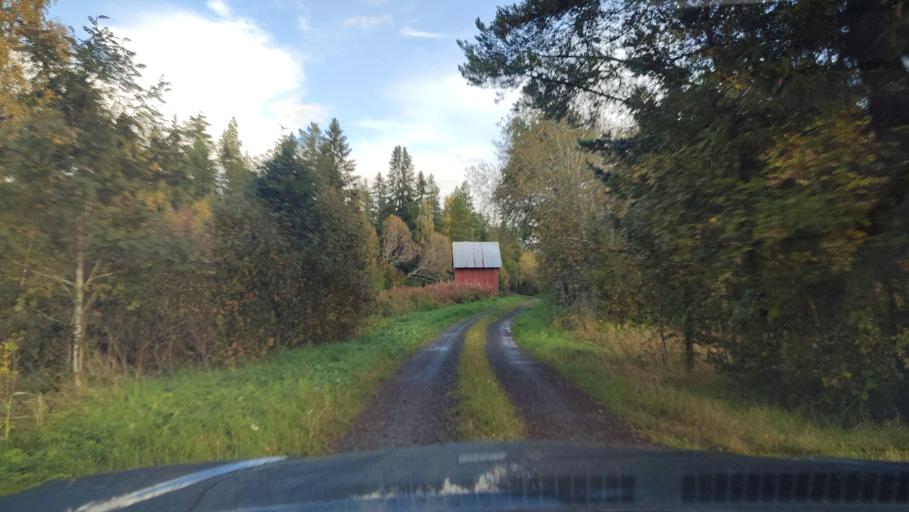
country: FI
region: Ostrobothnia
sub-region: Sydosterbotten
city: Kristinestad
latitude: 62.3064
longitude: 21.5019
